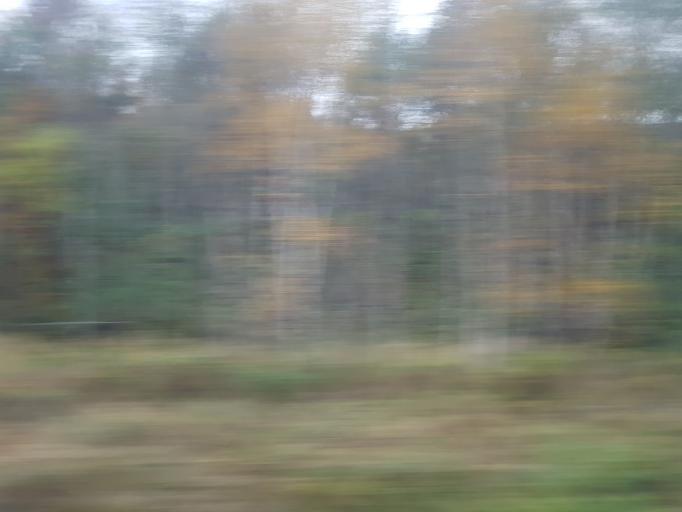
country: NO
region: Oppland
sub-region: Dovre
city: Dovre
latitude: 61.9250
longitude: 9.3309
